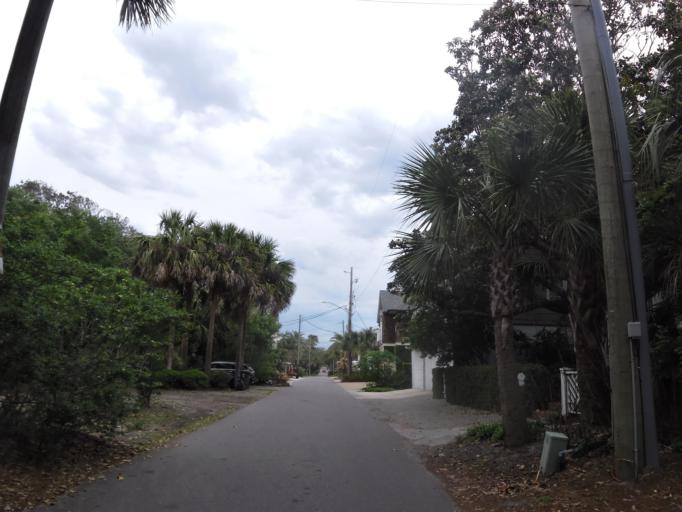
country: US
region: Florida
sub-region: Duval County
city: Atlantic Beach
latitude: 30.3447
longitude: -81.3977
